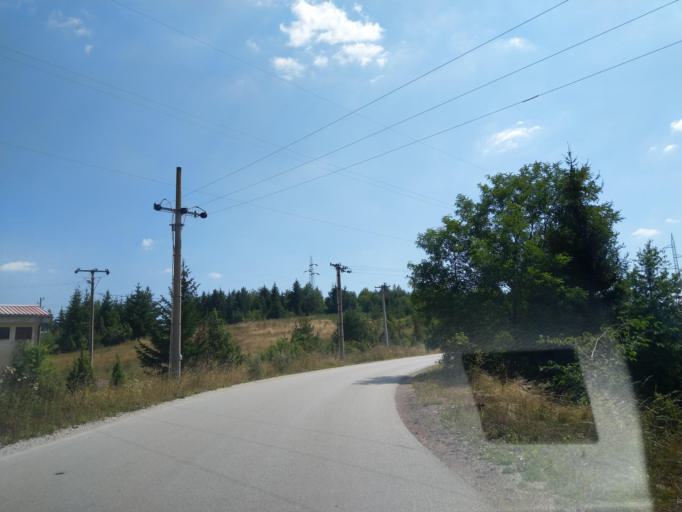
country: RS
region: Central Serbia
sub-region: Zlatiborski Okrug
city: Nova Varos
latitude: 43.4309
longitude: 19.8887
